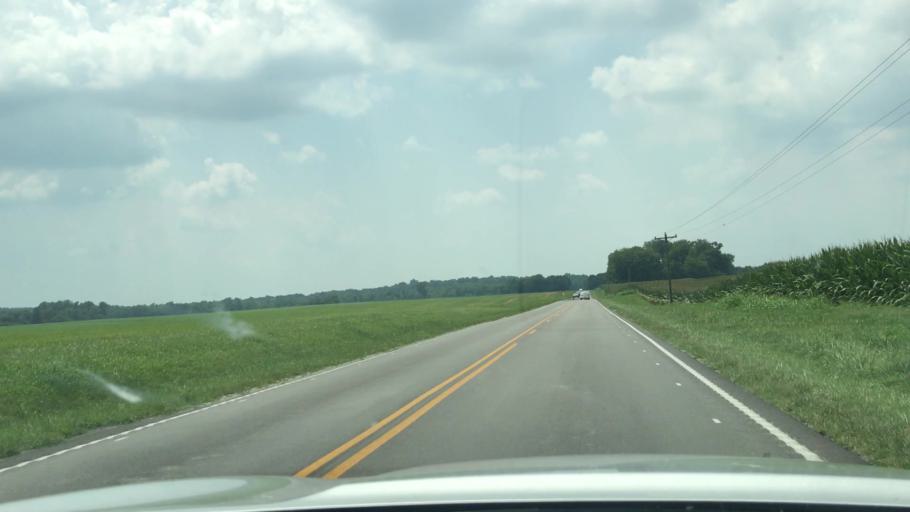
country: US
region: Kentucky
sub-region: Todd County
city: Guthrie
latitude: 36.7209
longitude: -87.0910
